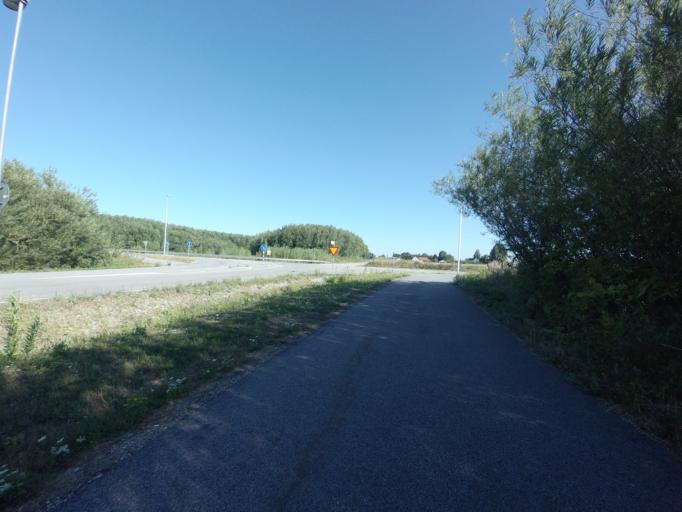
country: SE
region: Skane
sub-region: Trelleborgs Kommun
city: Skare
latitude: 55.4092
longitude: 13.0706
